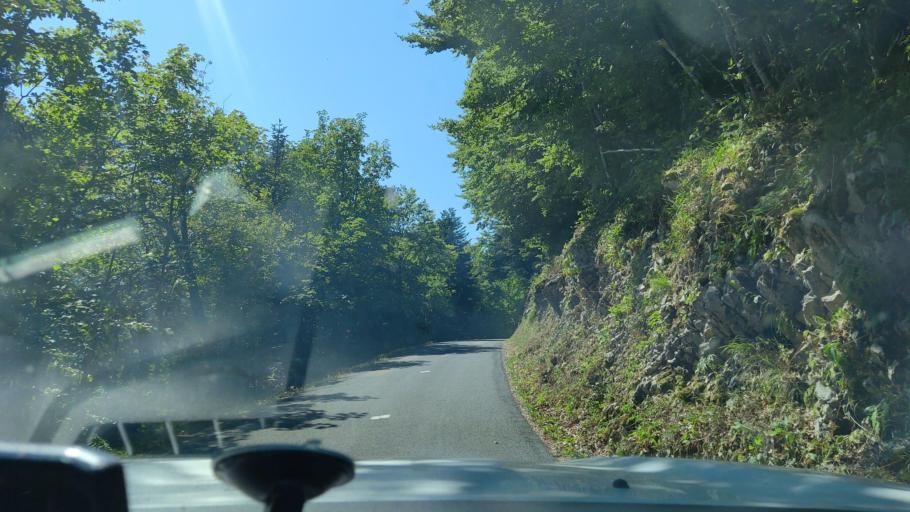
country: FR
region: Rhone-Alpes
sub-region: Departement de la Savoie
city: Le Bourget-du-Lac
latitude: 45.6442
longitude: 5.8257
